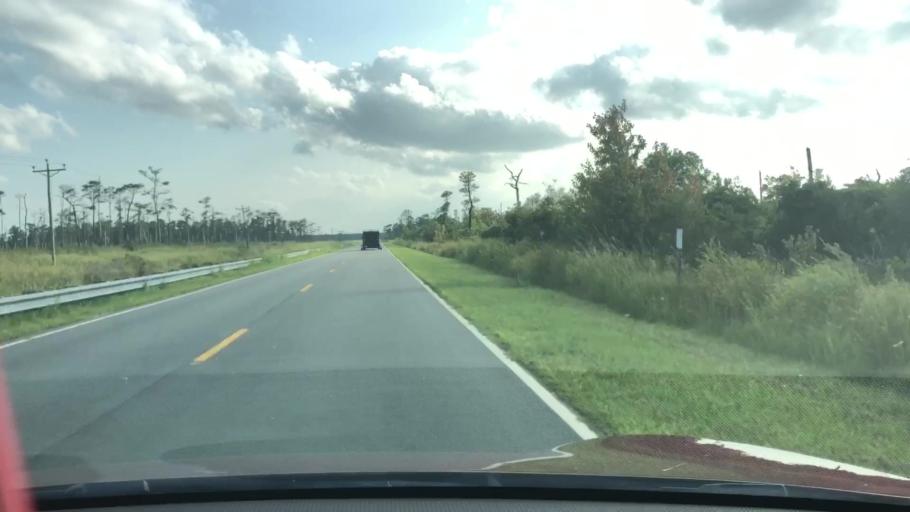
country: US
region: North Carolina
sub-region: Dare County
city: Wanchese
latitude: 35.6195
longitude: -75.7896
